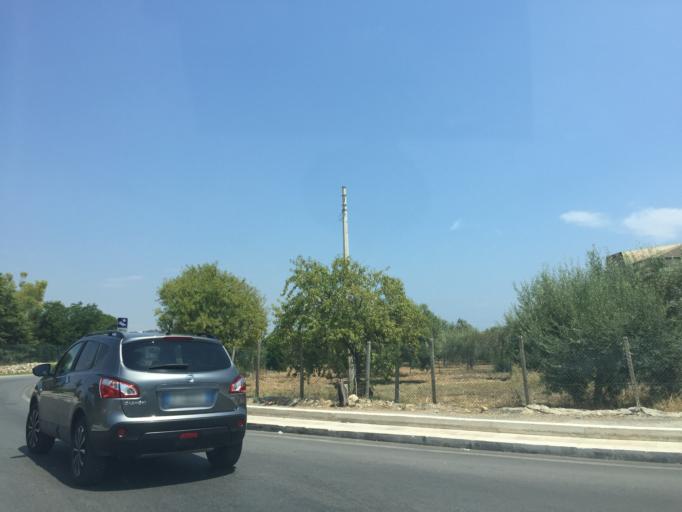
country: IT
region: Sicily
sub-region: Provincia di Siracusa
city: Avola
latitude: 36.9232
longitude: 15.1557
